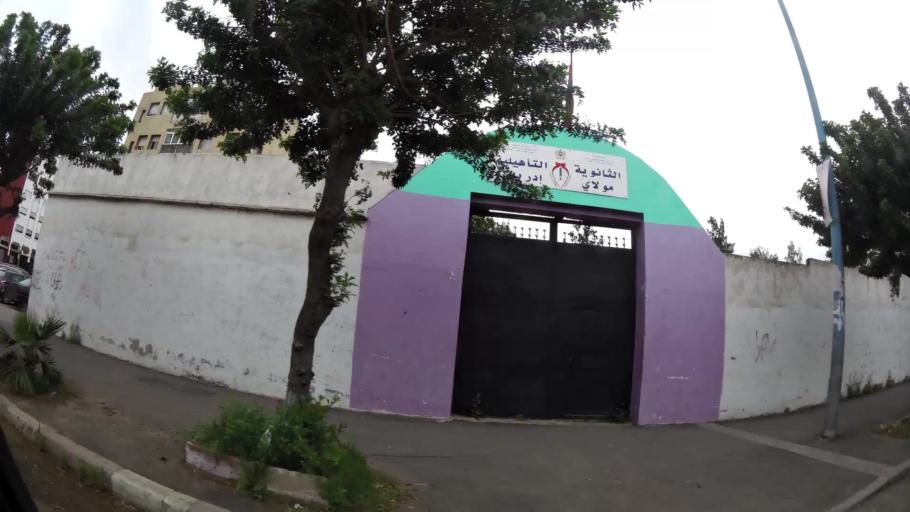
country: MA
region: Grand Casablanca
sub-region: Mediouna
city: Tit Mellil
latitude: 33.5683
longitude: -7.5472
